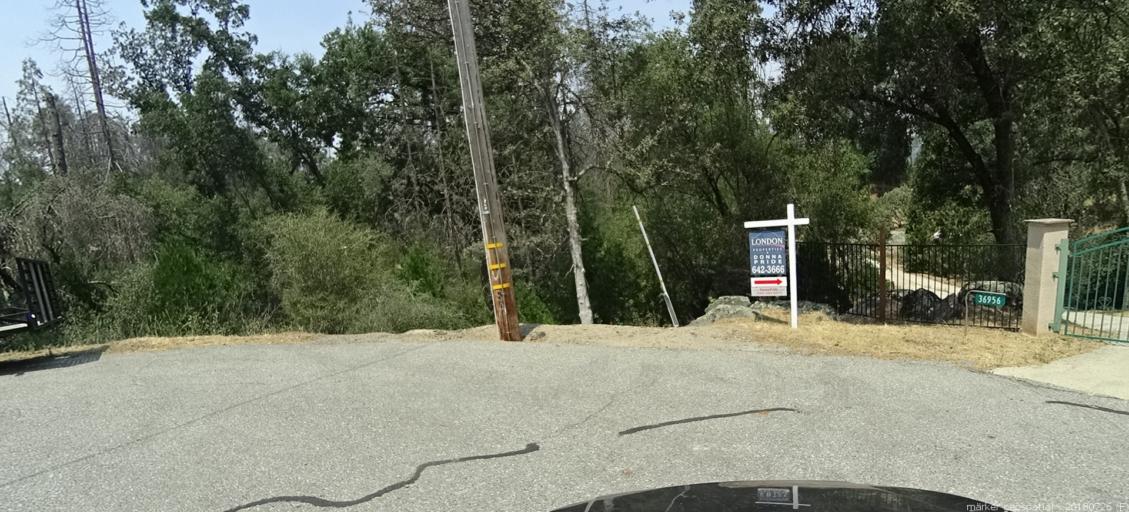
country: US
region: California
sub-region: Madera County
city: Oakhurst
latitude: 37.2850
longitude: -119.6485
